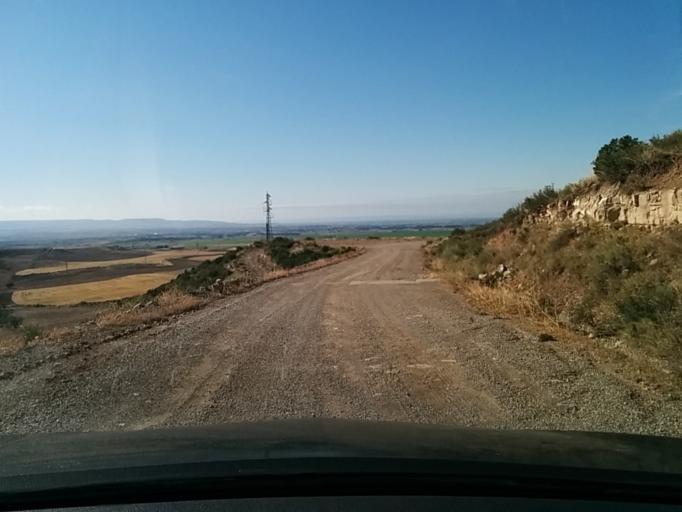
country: ES
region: Aragon
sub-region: Provincia de Zaragoza
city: Tauste
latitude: 42.0223
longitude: -1.3095
